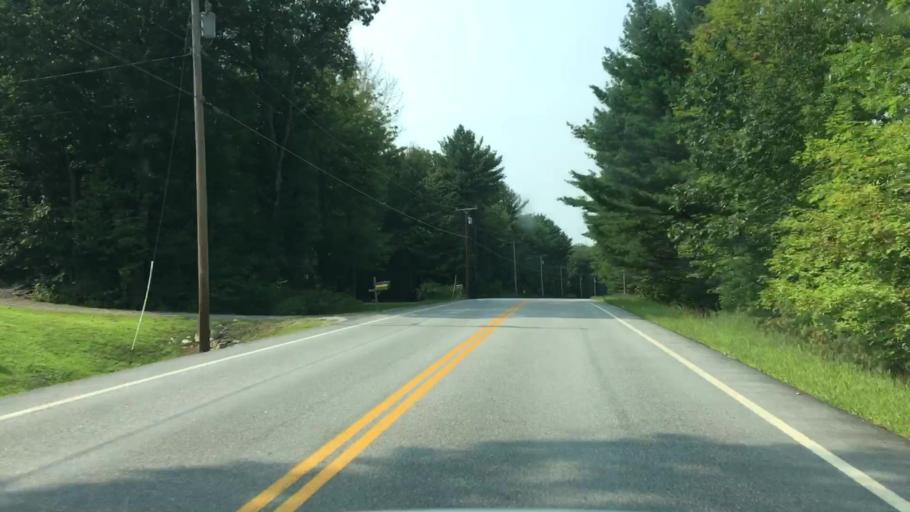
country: US
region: Maine
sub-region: Androscoggin County
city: Livermore
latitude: 44.3303
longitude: -70.2863
